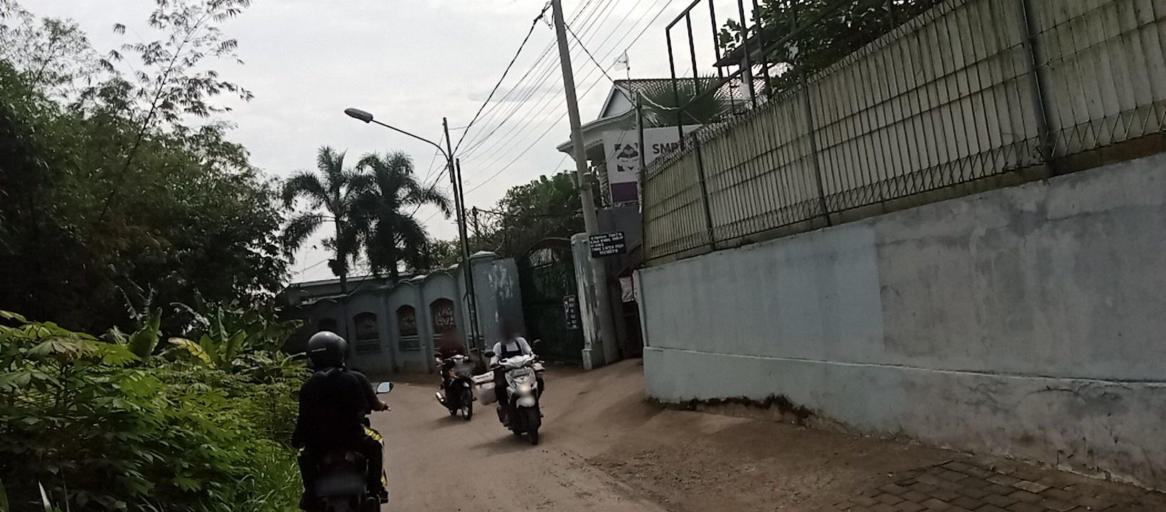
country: ID
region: West Java
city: Bogor
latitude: -6.5787
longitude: 106.8254
